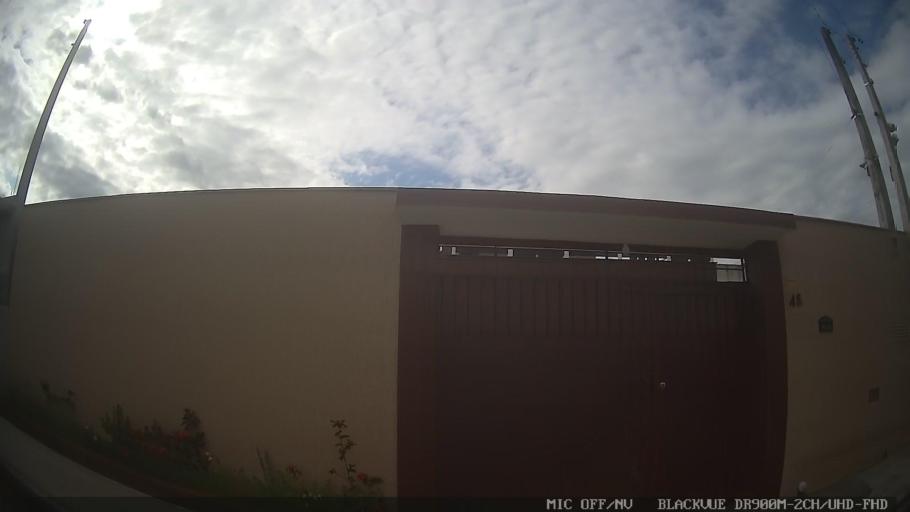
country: BR
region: Sao Paulo
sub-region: Sao Sebastiao
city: Sao Sebastiao
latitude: -23.7020
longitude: -45.4347
